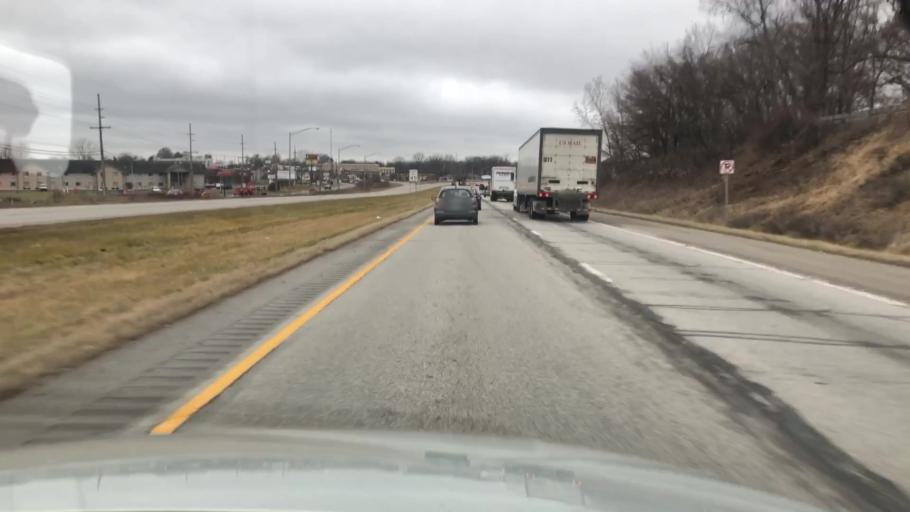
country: US
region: Indiana
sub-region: Kosciusko County
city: Winona Lake
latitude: 41.2354
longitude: -85.8088
